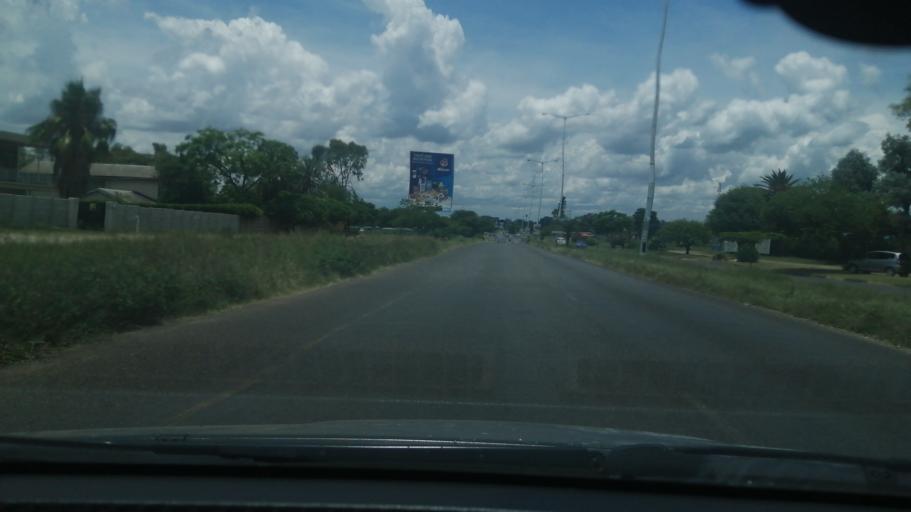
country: ZW
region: Harare
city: Harare
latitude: -17.8227
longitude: 31.0847
